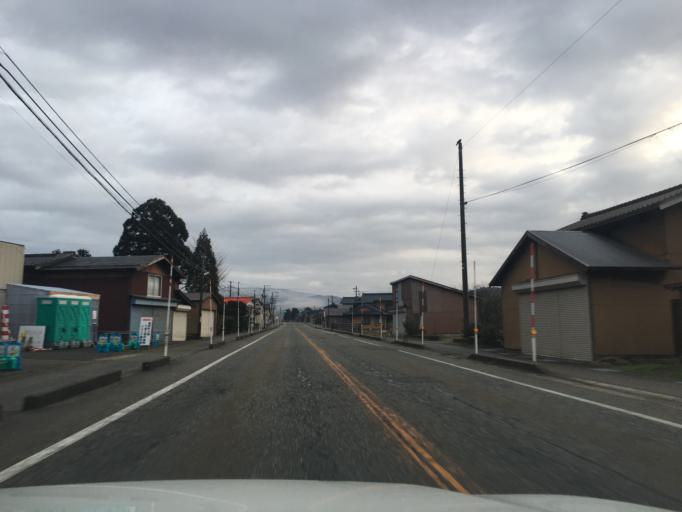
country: JP
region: Niigata
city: Murakami
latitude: 38.3115
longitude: 139.5468
